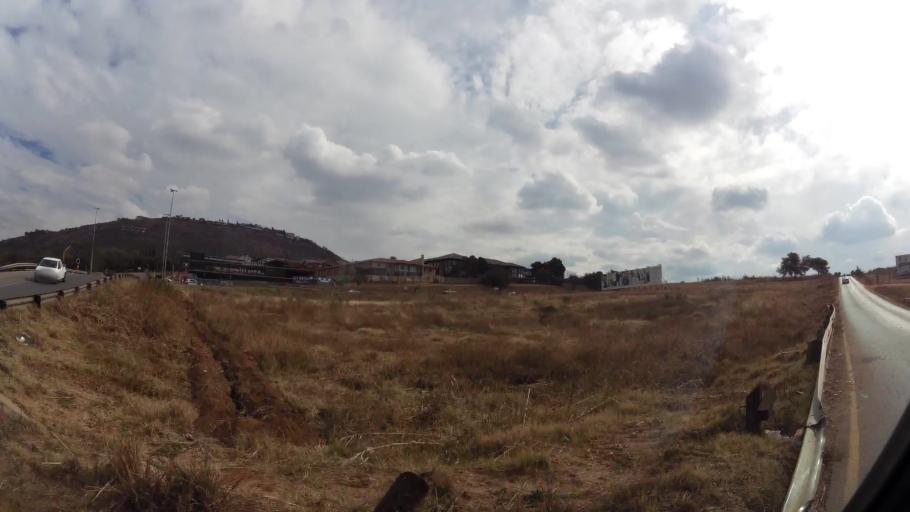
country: ZA
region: Gauteng
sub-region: City of Johannesburg Metropolitan Municipality
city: Roodepoort
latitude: -26.1057
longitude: 27.8825
